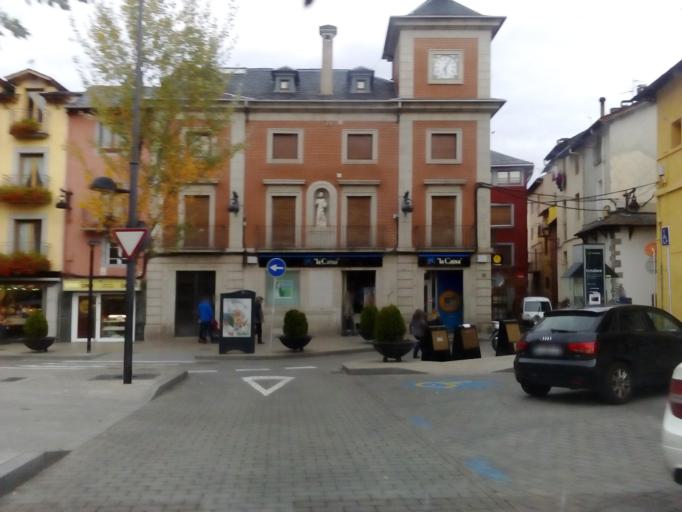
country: ES
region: Catalonia
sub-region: Provincia de Girona
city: Puigcerda
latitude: 42.4324
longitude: 1.9284
